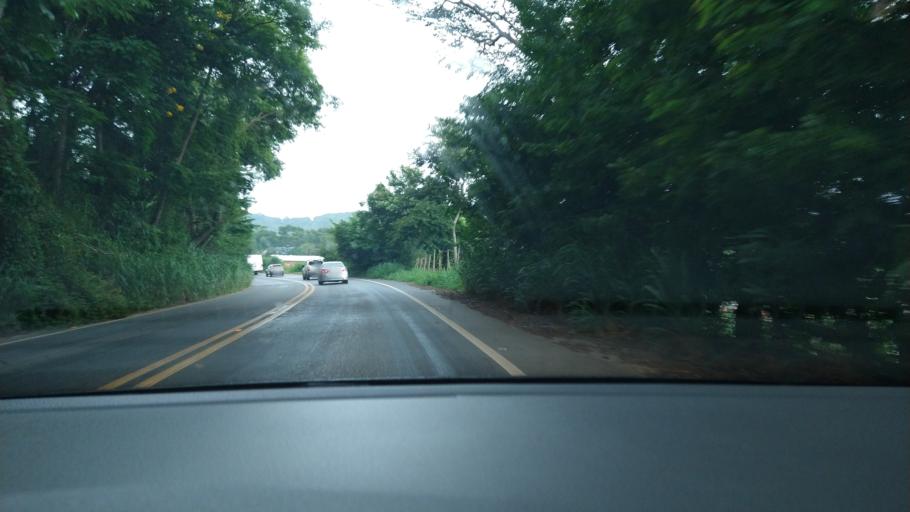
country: BR
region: Minas Gerais
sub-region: Vicosa
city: Vicosa
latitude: -20.6530
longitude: -42.8601
